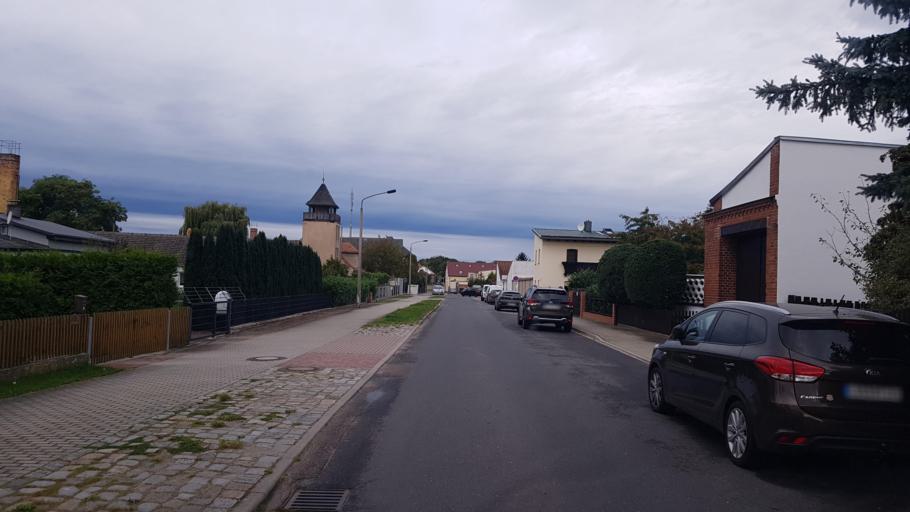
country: DE
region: Brandenburg
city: Golssen
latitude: 51.9692
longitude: 13.6052
